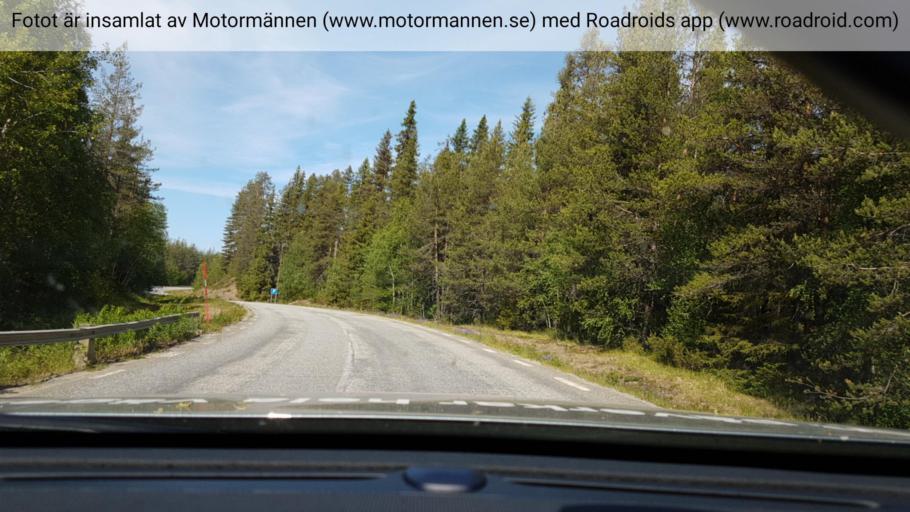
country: SE
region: Vaesterbotten
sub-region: Vilhelmina Kommun
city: Sjoberg
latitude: 64.6272
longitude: 15.8267
